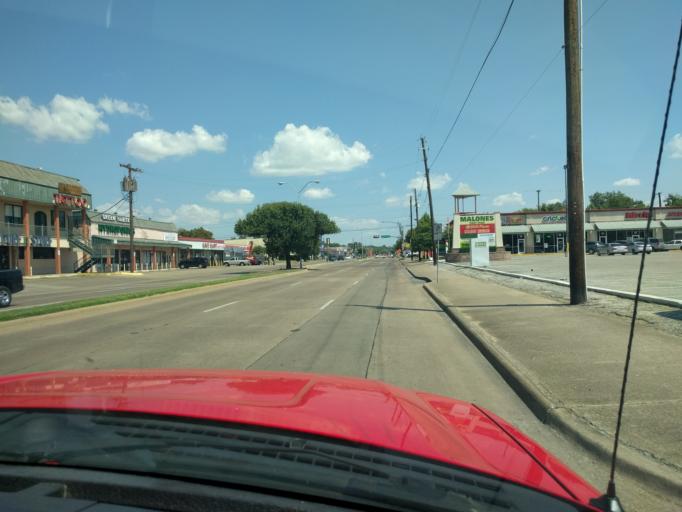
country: US
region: Texas
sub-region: Dallas County
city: Dallas
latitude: 32.7944
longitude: -96.7644
